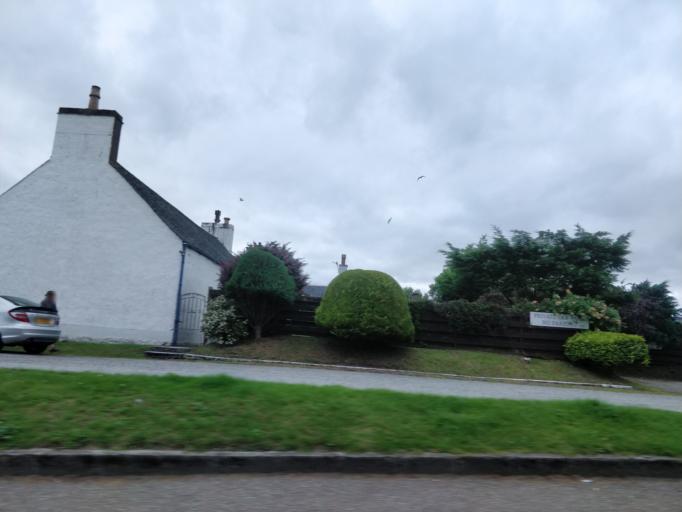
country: GB
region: Scotland
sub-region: Highland
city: Ullapool
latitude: 57.8970
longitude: -5.1551
